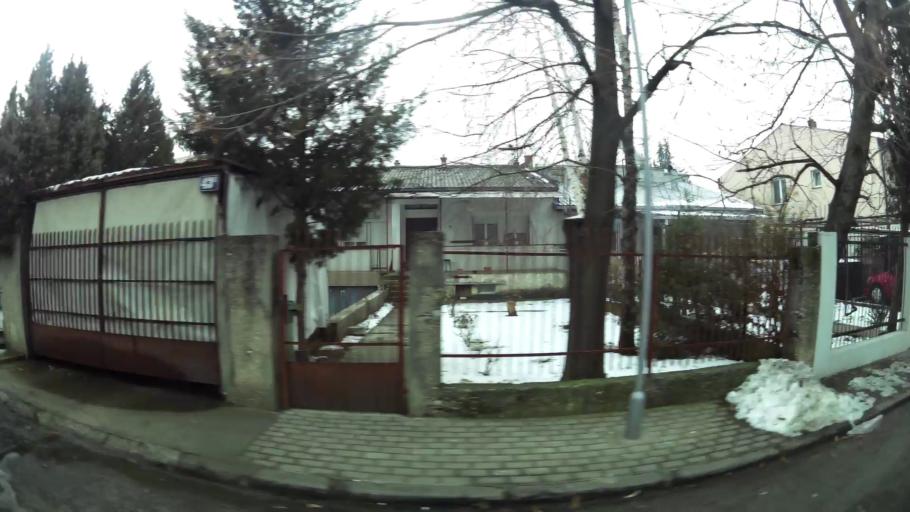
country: MK
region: Cair
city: Cair
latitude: 42.0176
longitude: 21.4498
